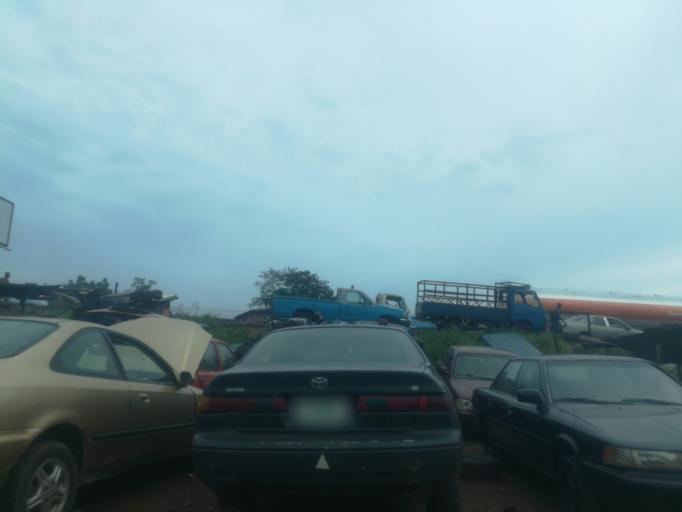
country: NG
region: Oyo
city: Ibadan
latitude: 7.3937
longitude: 3.9376
